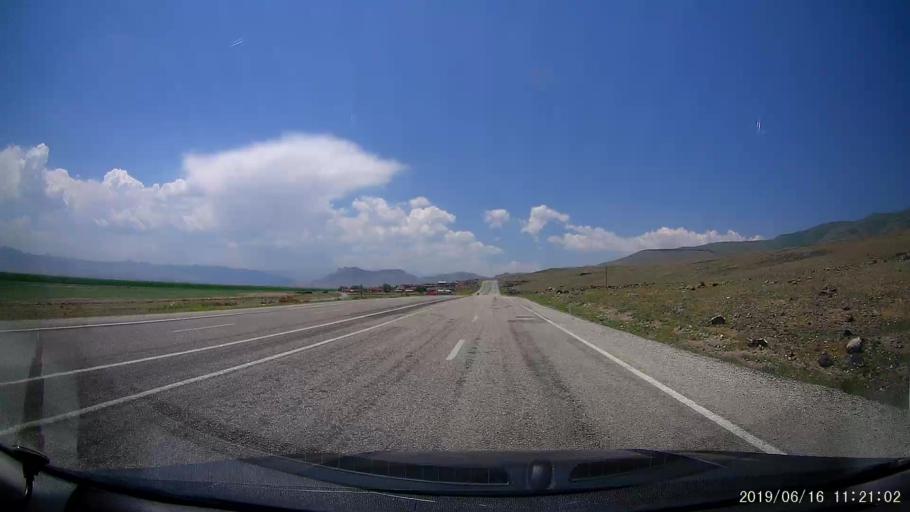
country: TR
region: Agri
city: Dogubayazit
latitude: 39.6972
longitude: 44.0775
